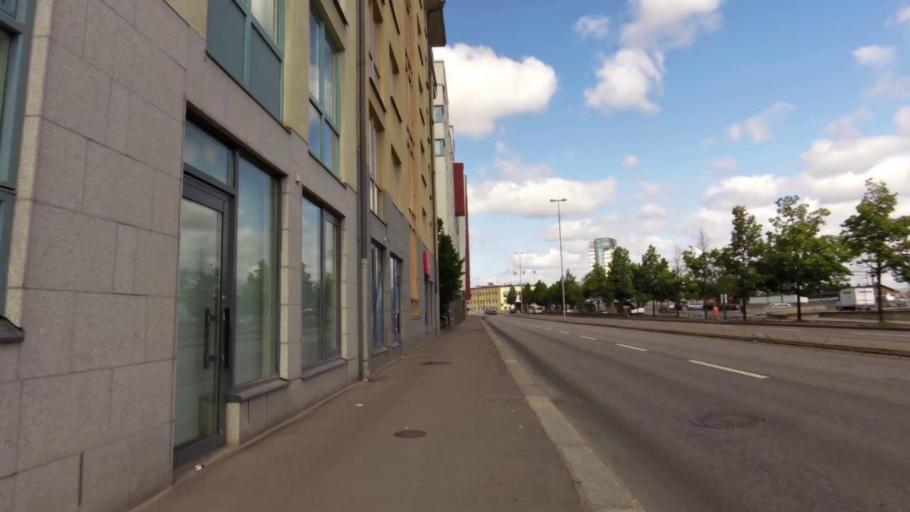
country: SE
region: OEstergoetland
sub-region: Linkopings Kommun
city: Linkoping
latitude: 58.4182
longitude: 15.6206
